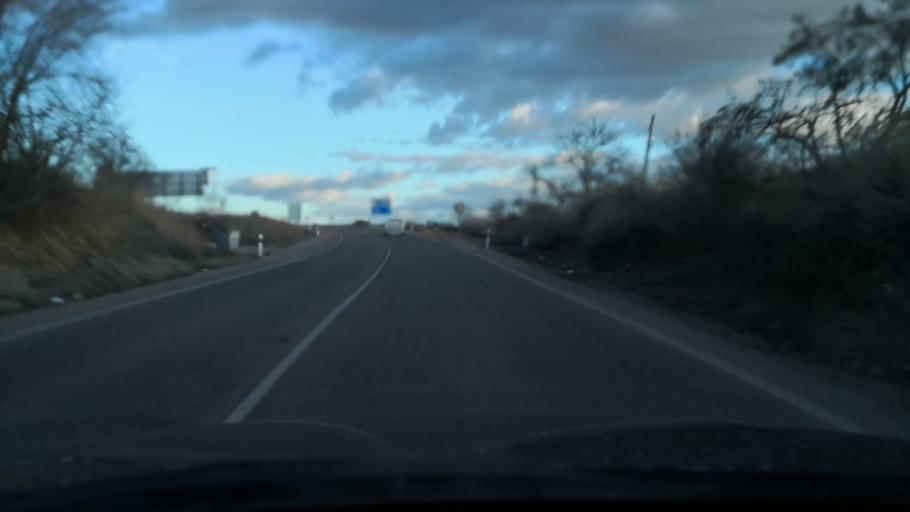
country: ES
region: Castille and Leon
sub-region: Provincia de Valladolid
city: Medina del Campo
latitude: 41.3115
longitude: -4.9025
